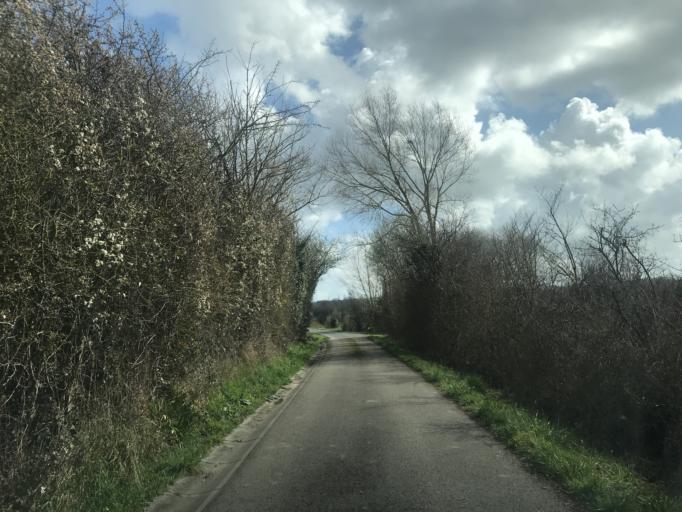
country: FR
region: Lower Normandy
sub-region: Departement du Calvados
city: Dives-sur-Mer
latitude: 49.2670
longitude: -0.1031
